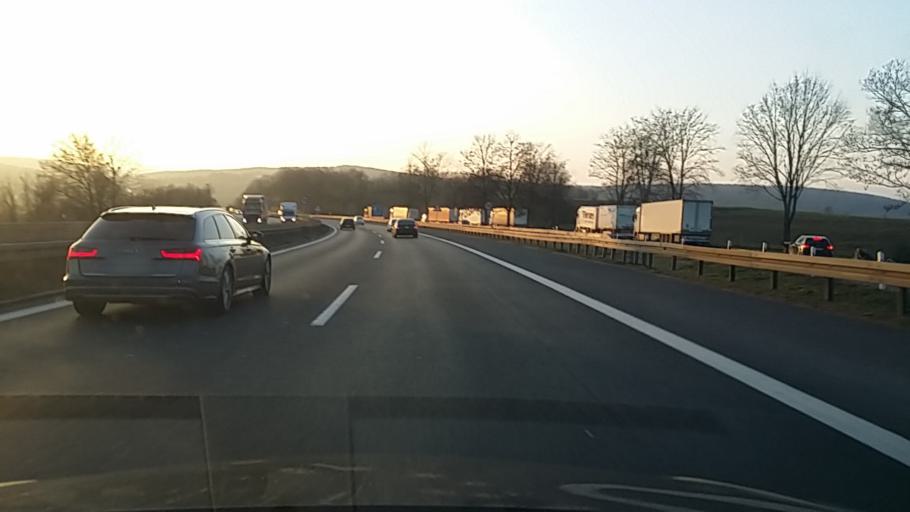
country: DE
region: Bavaria
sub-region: Upper Palatinate
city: Sinzing
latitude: 49.0014
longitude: 12.0488
